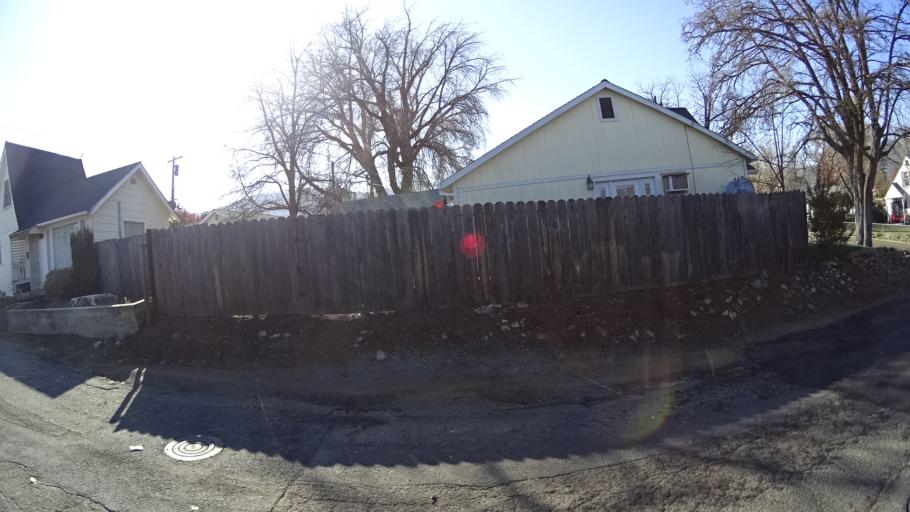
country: US
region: California
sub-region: Siskiyou County
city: Yreka
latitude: 41.7352
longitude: -122.6293
